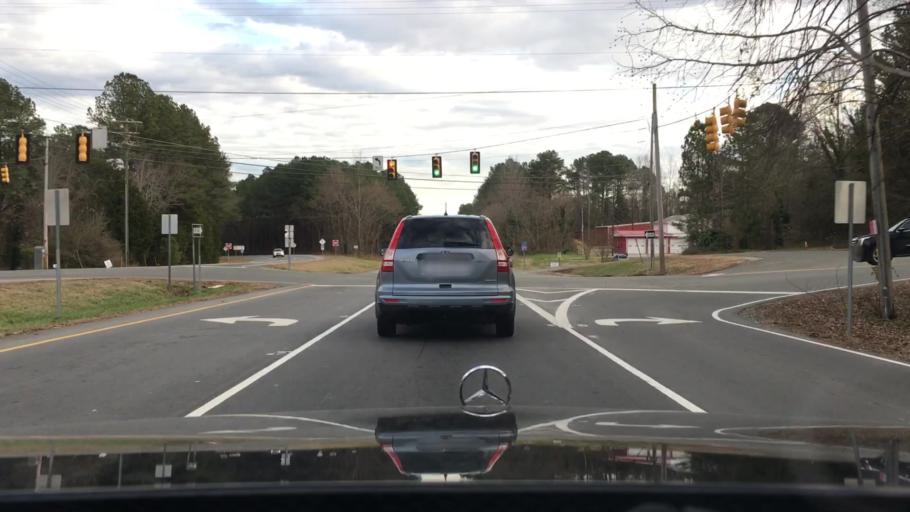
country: US
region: North Carolina
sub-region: Orange County
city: Hillsborough
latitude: 36.0413
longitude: -79.0148
